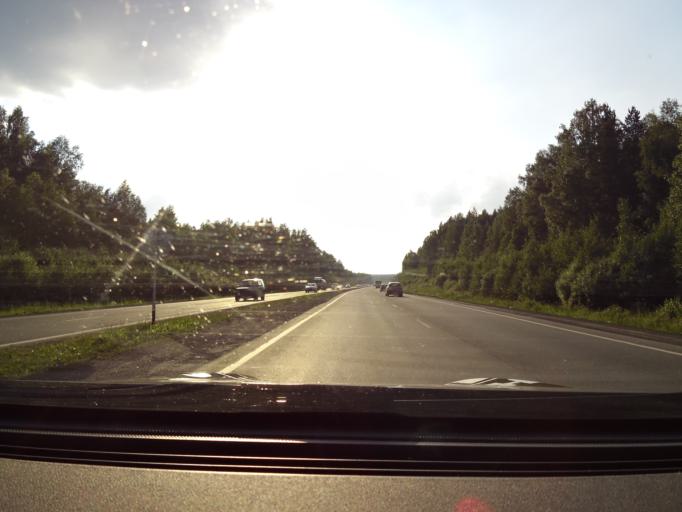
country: RU
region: Sverdlovsk
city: Talitsa
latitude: 56.8408
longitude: 60.1046
